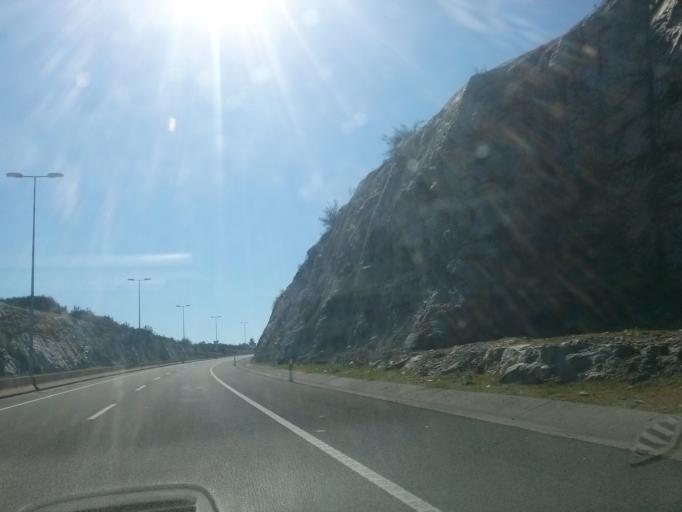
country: ES
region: Galicia
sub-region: Provincia de Lugo
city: Lugo
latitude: 43.0233
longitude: -7.5284
